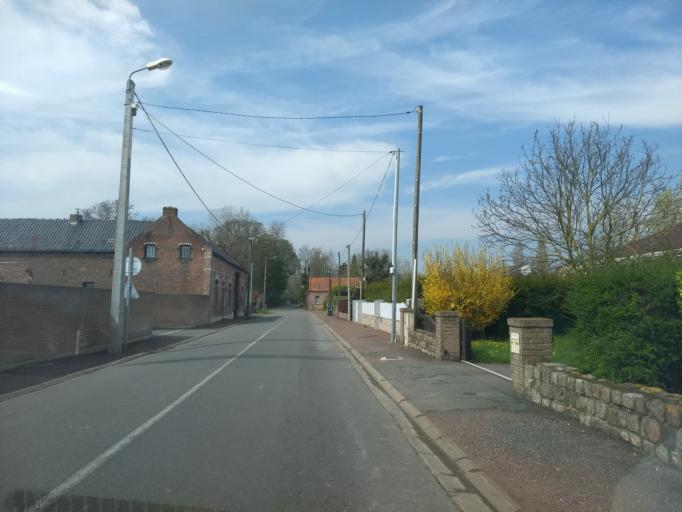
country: FR
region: Nord-Pas-de-Calais
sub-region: Departement du Nord
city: Guesnain
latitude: 50.3257
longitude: 3.1493
